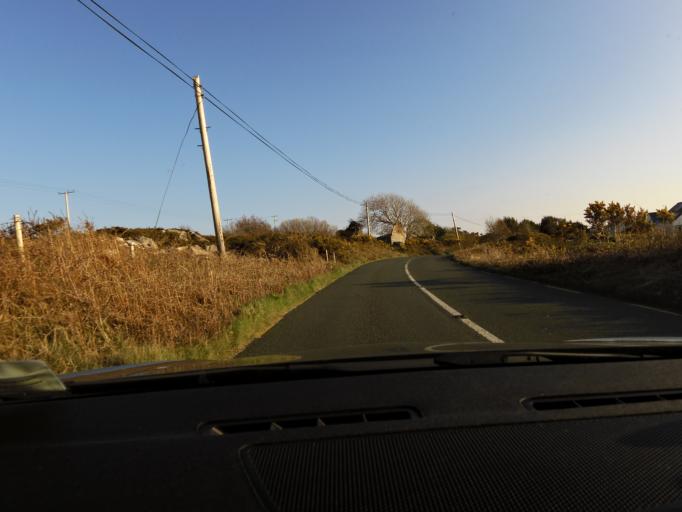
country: IE
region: Connaught
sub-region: County Galway
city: Oughterard
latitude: 53.2954
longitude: -9.5497
